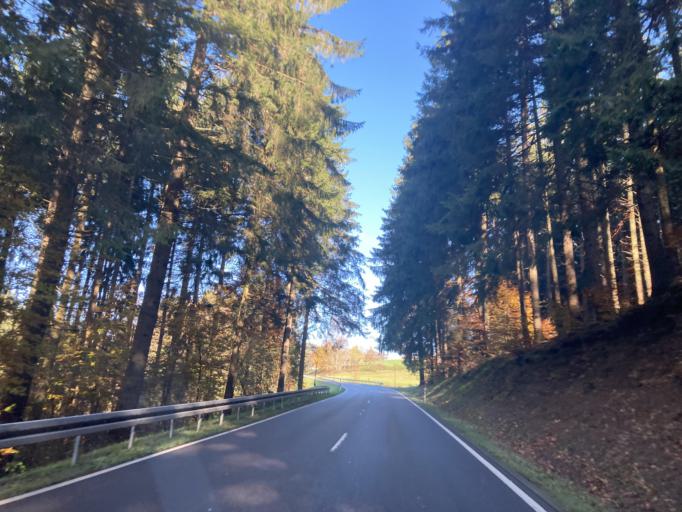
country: DE
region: Baden-Wuerttemberg
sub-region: Freiburg Region
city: Elzach
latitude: 48.2107
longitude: 8.0872
